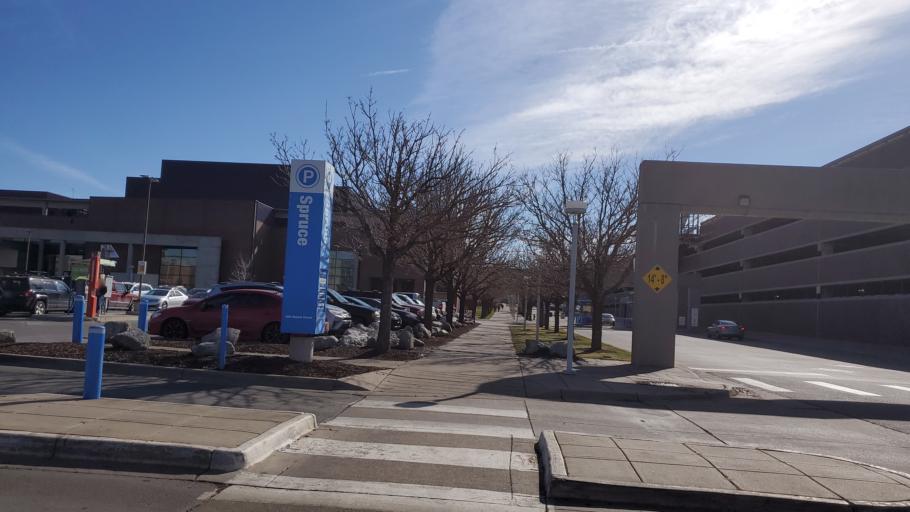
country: US
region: Colorado
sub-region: Denver County
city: Denver
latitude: 39.7446
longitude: -105.0075
